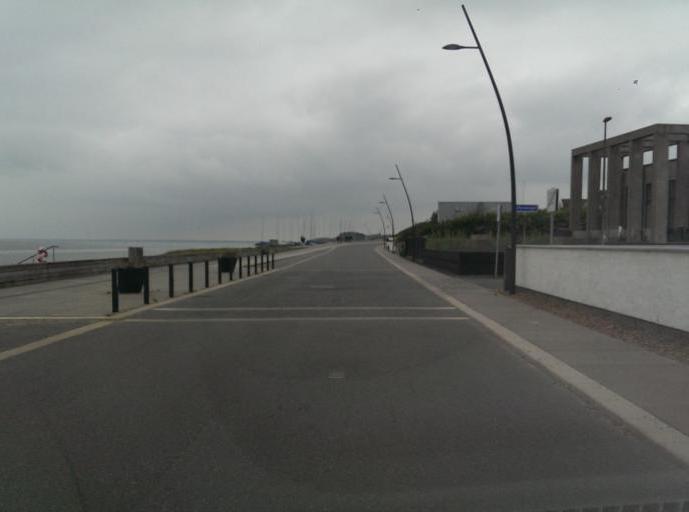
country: DK
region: South Denmark
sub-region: Fano Kommune
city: Nordby
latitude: 55.5260
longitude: 8.3502
